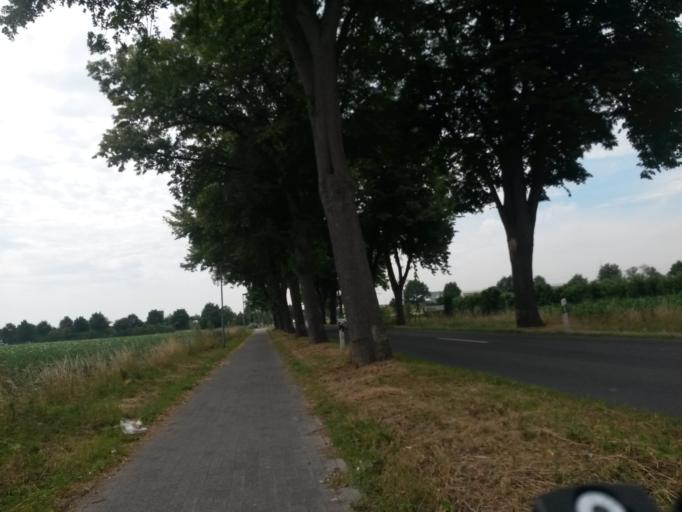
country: DE
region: North Rhine-Westphalia
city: Kempen
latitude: 51.3744
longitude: 6.4431
